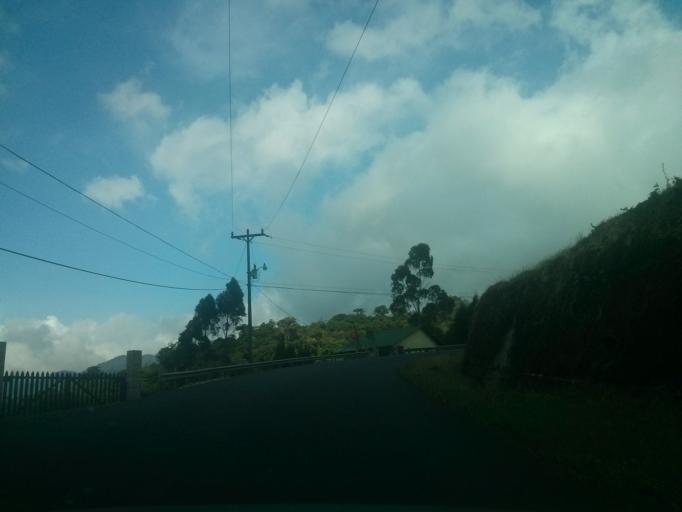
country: CR
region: Heredia
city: Santo Domingo
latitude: 10.1577
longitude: -84.1497
